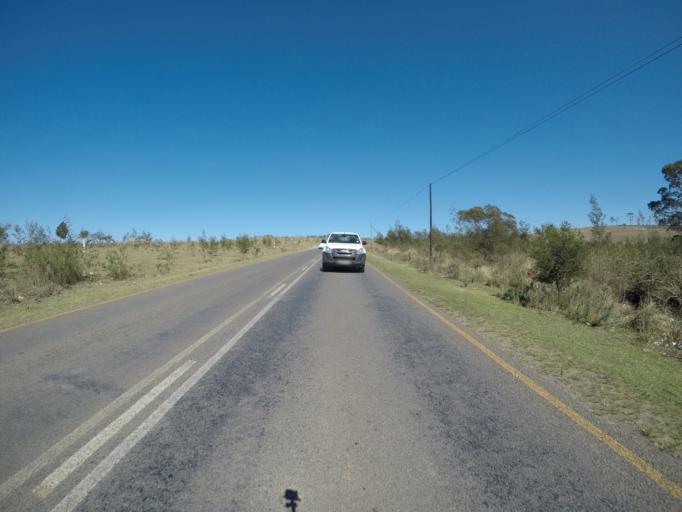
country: ZA
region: Eastern Cape
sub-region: OR Tambo District Municipality
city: Mthatha
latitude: -31.8068
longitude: 28.7588
